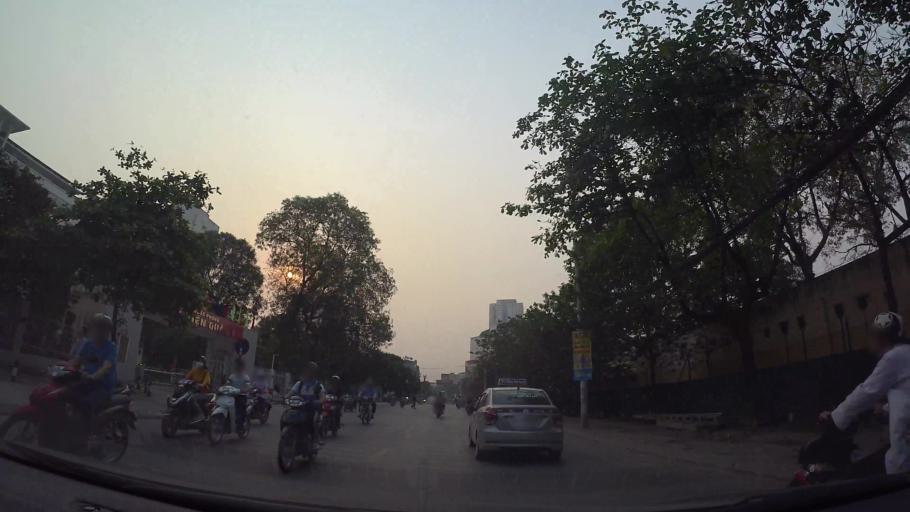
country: VN
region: Ha Noi
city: Ha Dong
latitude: 20.9673
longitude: 105.7889
